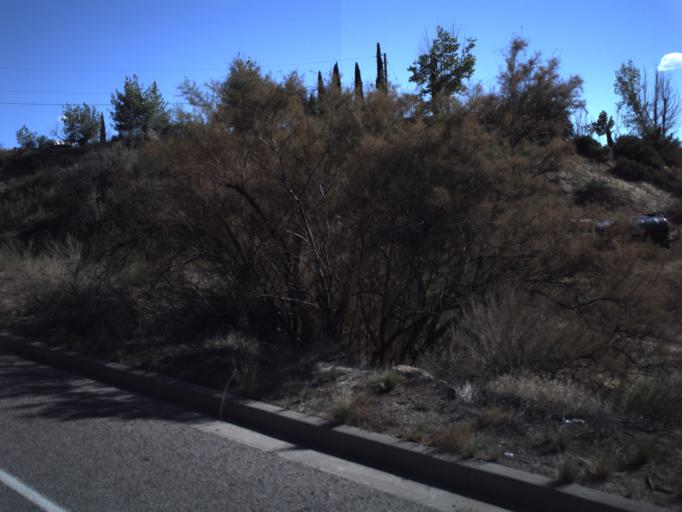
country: US
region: Utah
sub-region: Washington County
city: LaVerkin
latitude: 37.2159
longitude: -113.2727
